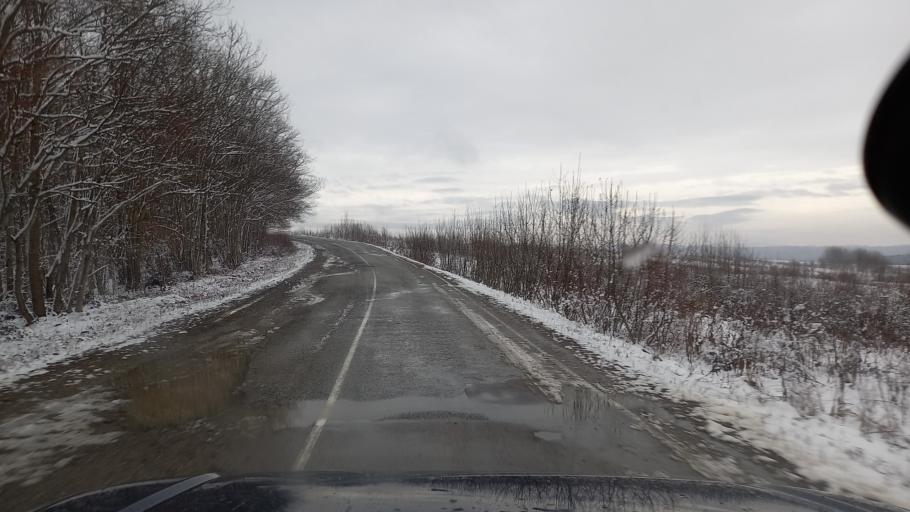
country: RU
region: Adygeya
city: Abadzekhskaya
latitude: 44.3524
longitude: 40.3680
